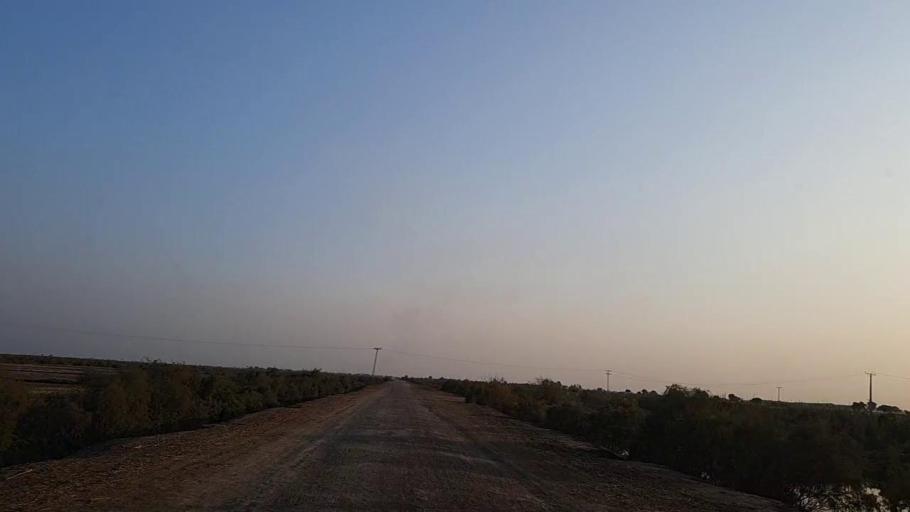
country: PK
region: Sindh
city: Shahdadpur
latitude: 25.9895
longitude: 68.4948
